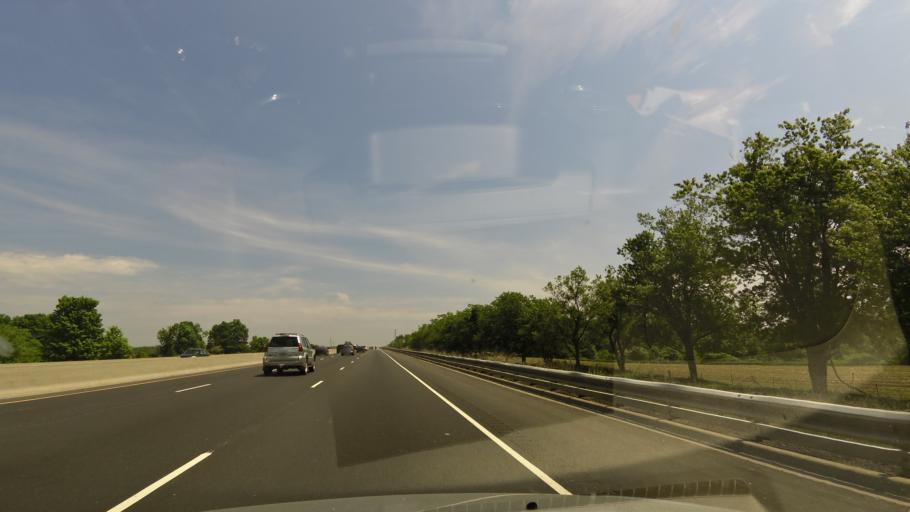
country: CA
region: Ontario
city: Oshawa
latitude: 43.9125
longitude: -78.5759
